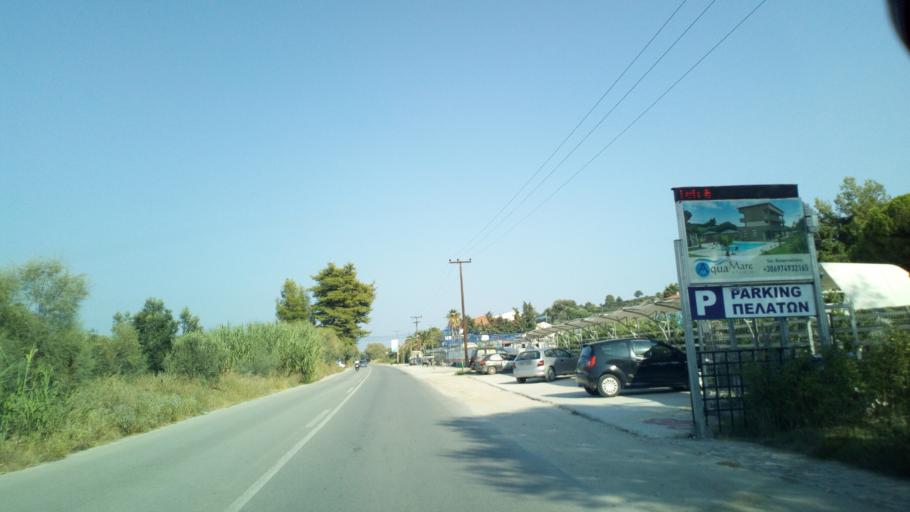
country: GR
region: Central Macedonia
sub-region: Nomos Chalkidikis
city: Pefkochori
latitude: 39.9773
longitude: 23.6534
